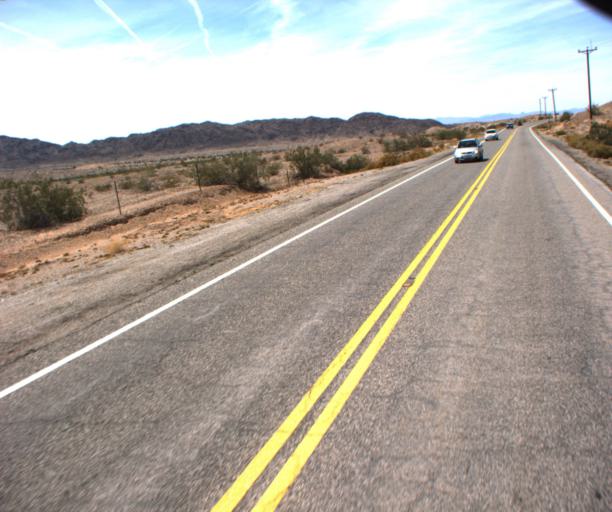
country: US
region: Arizona
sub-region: La Paz County
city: Parker
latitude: 34.0064
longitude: -114.2394
